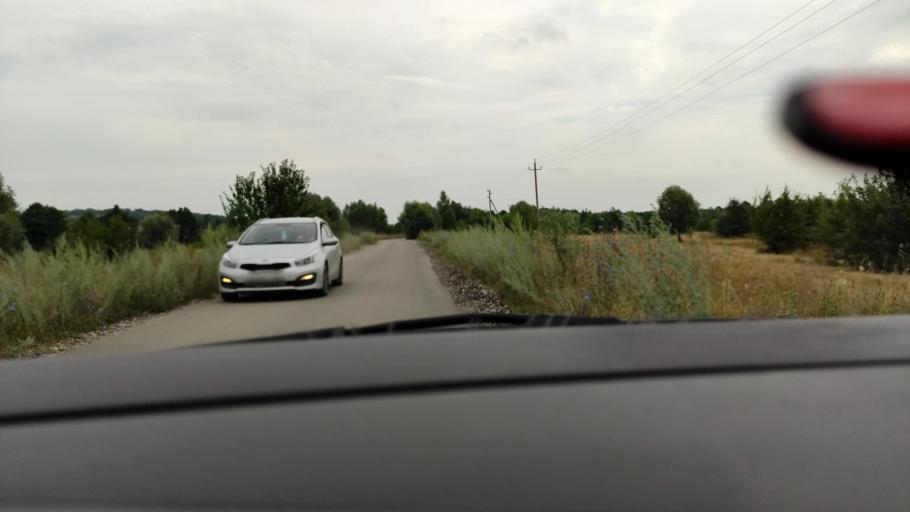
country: RU
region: Voronezj
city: Ramon'
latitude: 51.9016
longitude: 39.3506
